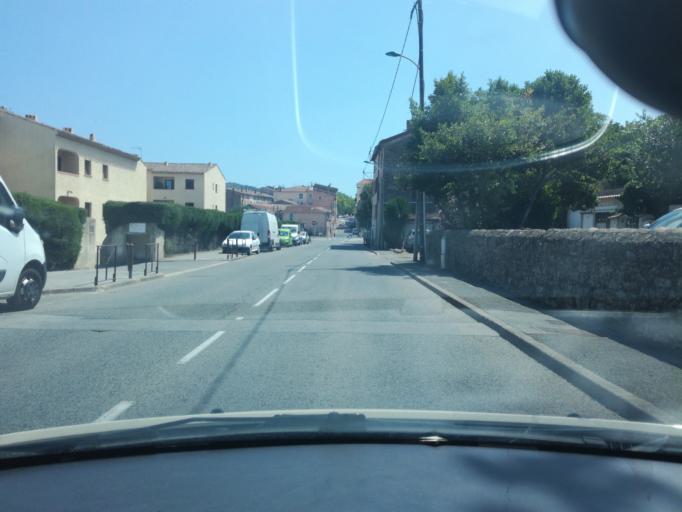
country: FR
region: Provence-Alpes-Cote d'Azur
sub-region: Departement du Var
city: Le Muy
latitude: 43.4758
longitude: 6.5667
